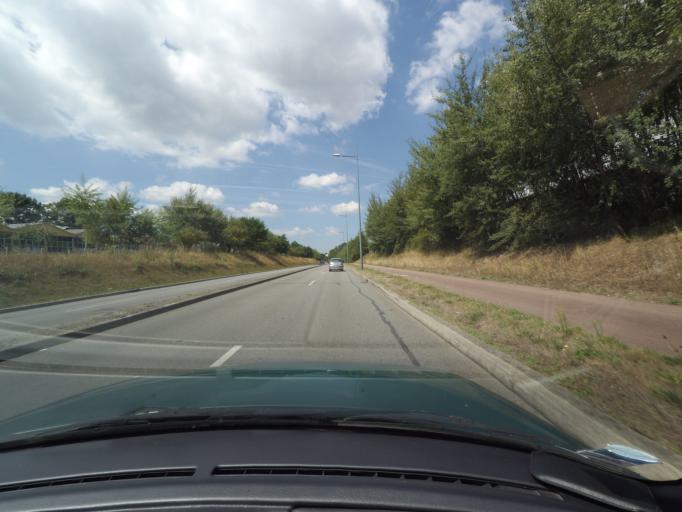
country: FR
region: Limousin
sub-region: Departement de la Haute-Vienne
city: Condat-sur-Vienne
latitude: 45.8050
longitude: 1.2728
